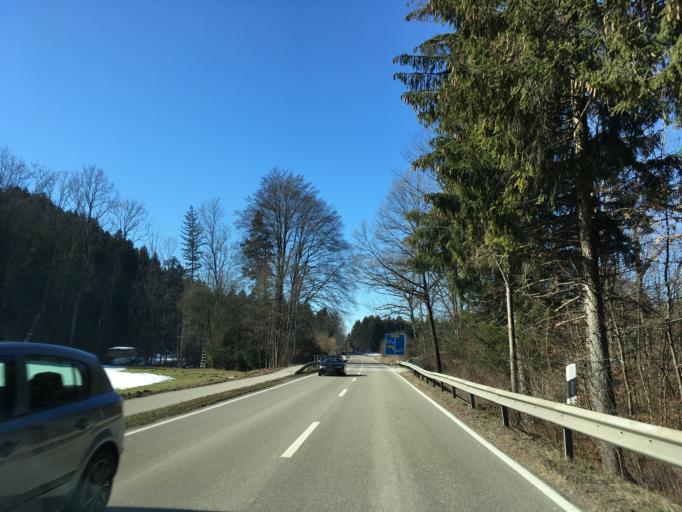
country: DE
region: Bavaria
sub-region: Upper Bavaria
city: Samerberg
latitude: 47.7957
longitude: 12.2186
